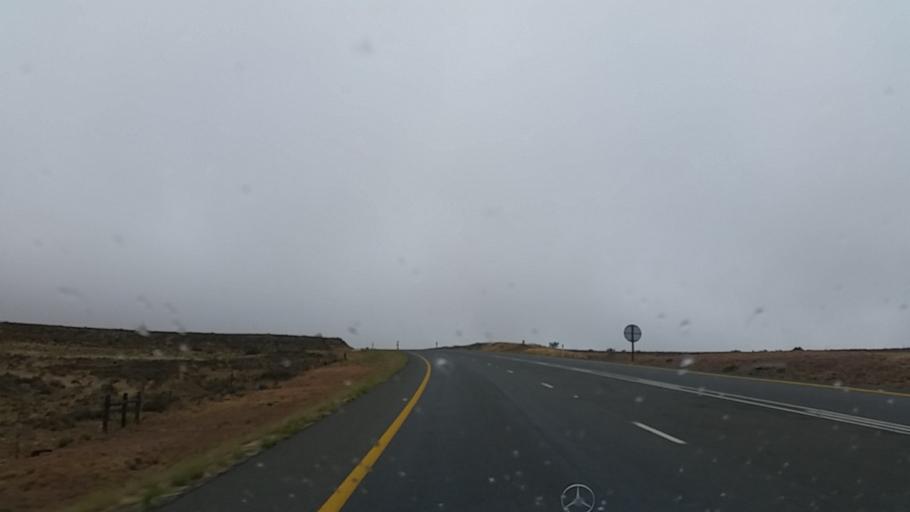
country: ZA
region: Eastern Cape
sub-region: Cacadu District Municipality
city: Graaff-Reinet
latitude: -31.9501
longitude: 24.7256
